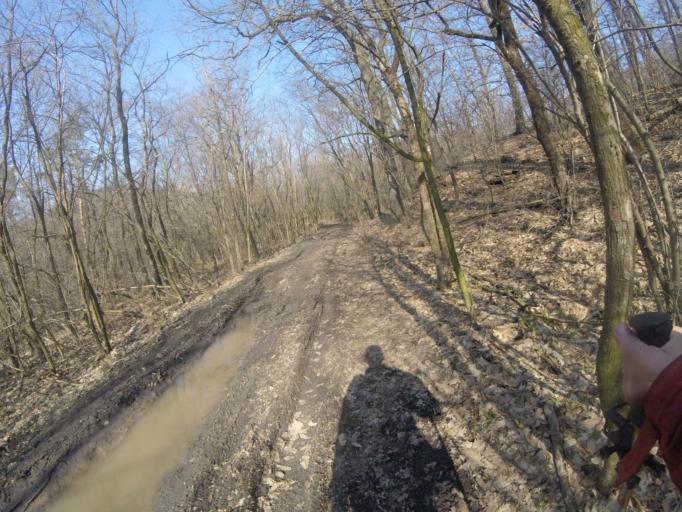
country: HU
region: Komarom-Esztergom
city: Nyergesujfalu
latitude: 47.7254
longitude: 18.5755
